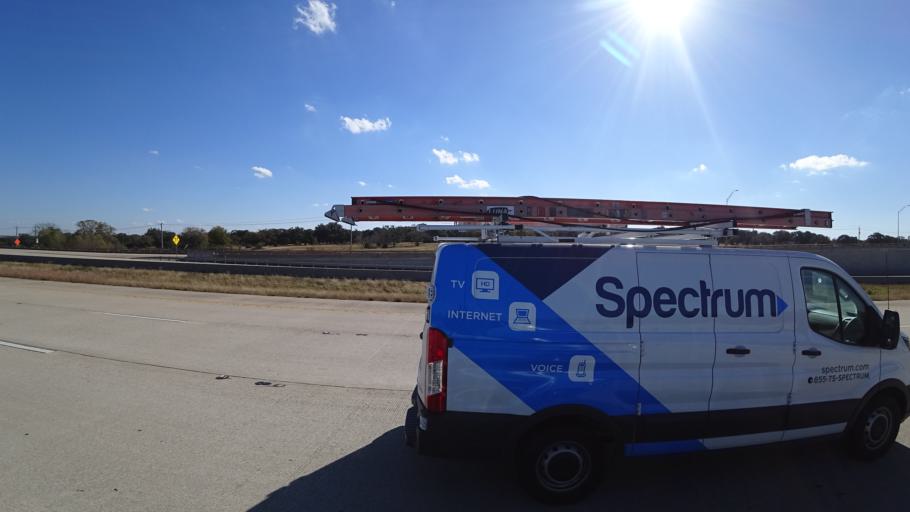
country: US
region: Texas
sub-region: Williamson County
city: Brushy Creek
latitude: 30.4813
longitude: -97.7496
